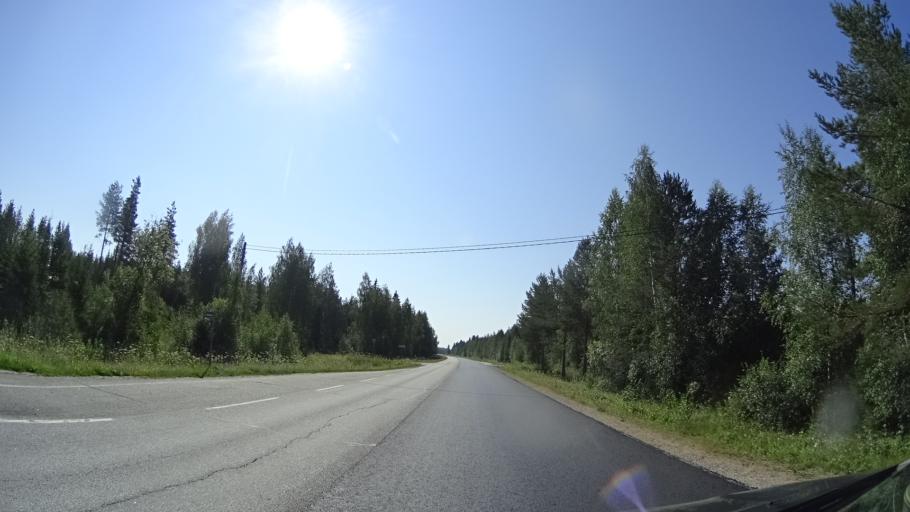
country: FI
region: North Karelia
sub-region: Joensuu
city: Juuka
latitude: 63.2272
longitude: 29.2900
